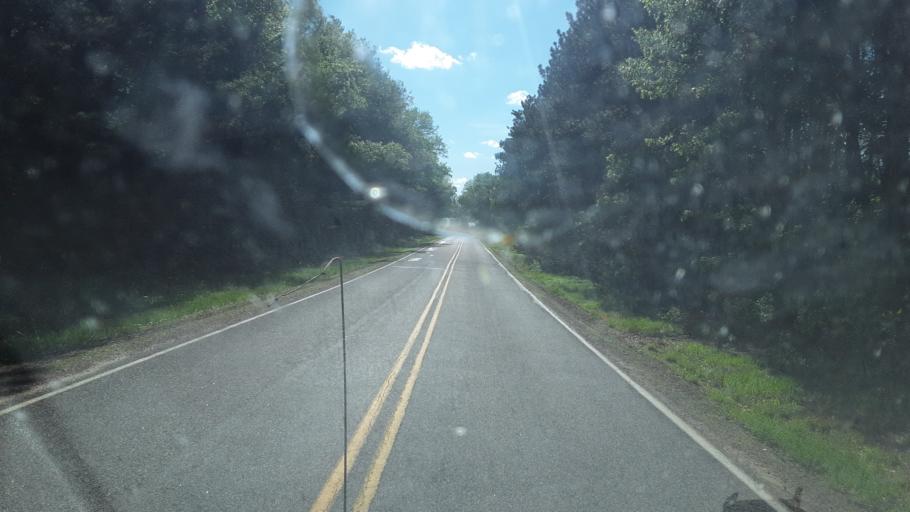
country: US
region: Wisconsin
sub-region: Wood County
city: Nekoosa
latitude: 44.3069
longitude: -90.1268
